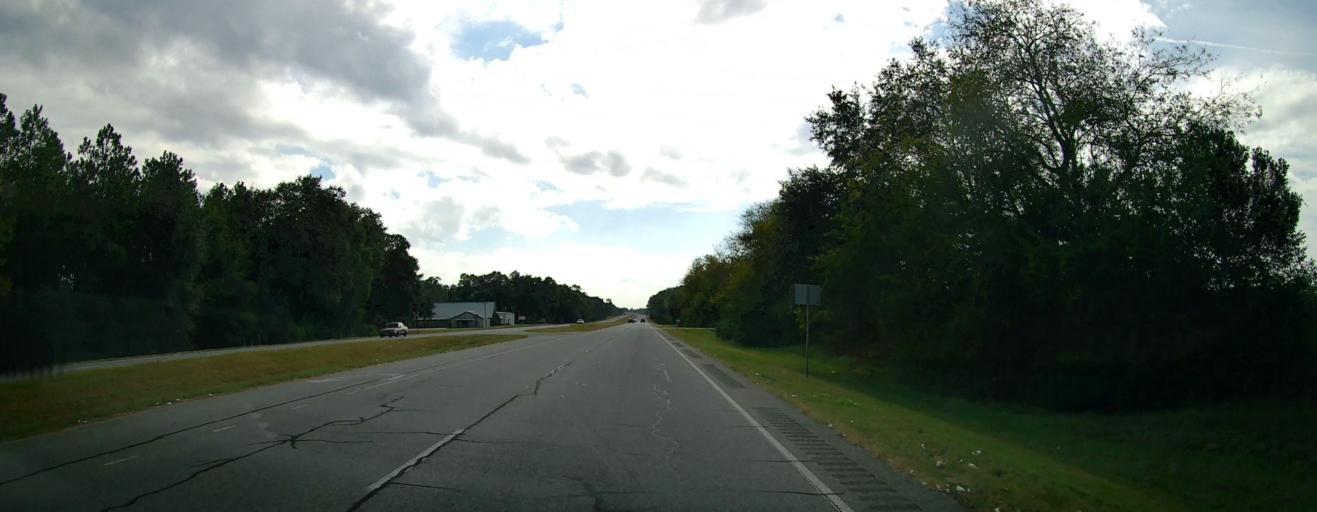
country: US
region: Georgia
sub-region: Mitchell County
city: Camilla
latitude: 31.3035
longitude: -84.1800
